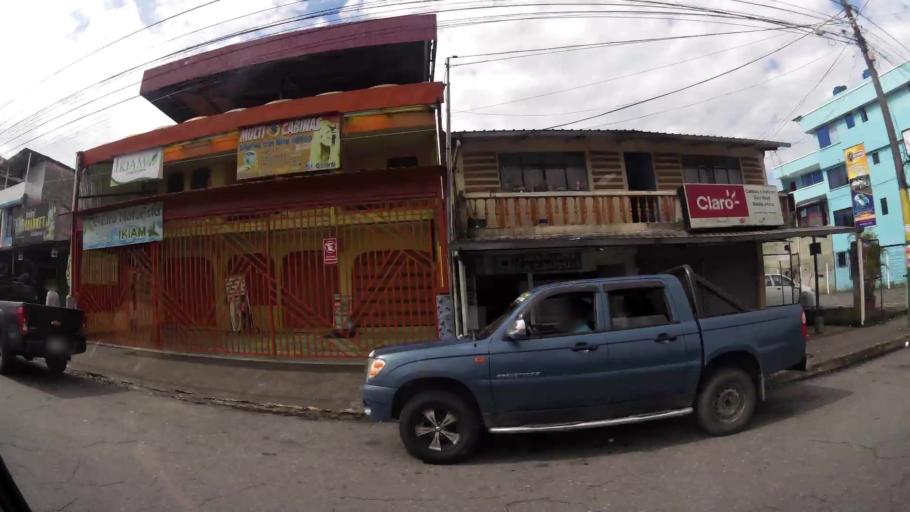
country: EC
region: Pastaza
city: Puyo
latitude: -1.4904
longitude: -78.0064
